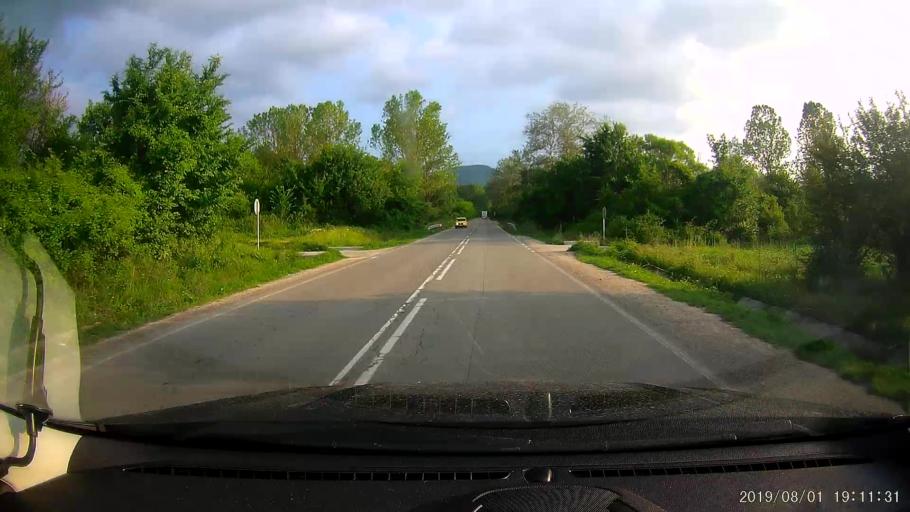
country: BG
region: Shumen
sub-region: Obshtina Smyadovo
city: Smyadovo
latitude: 42.9734
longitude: 26.9604
